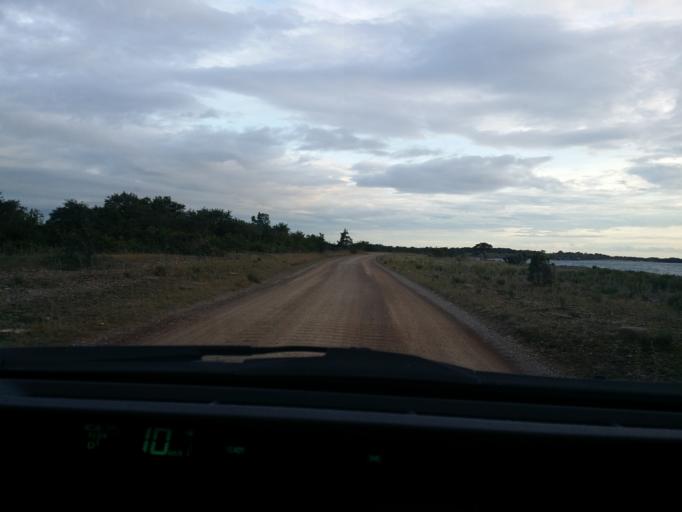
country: SE
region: Kalmar
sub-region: Borgholms Kommun
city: Borgholm
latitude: 57.2125
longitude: 16.9405
